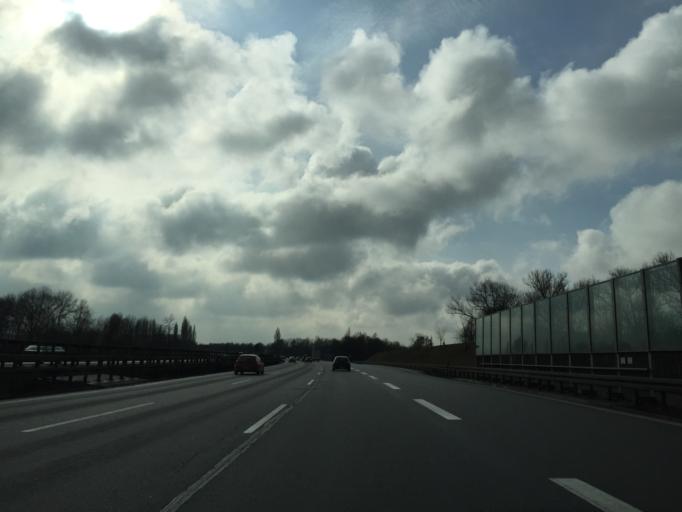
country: DE
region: Bavaria
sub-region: Upper Bavaria
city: Ingolstadt
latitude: 48.7561
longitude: 11.4572
